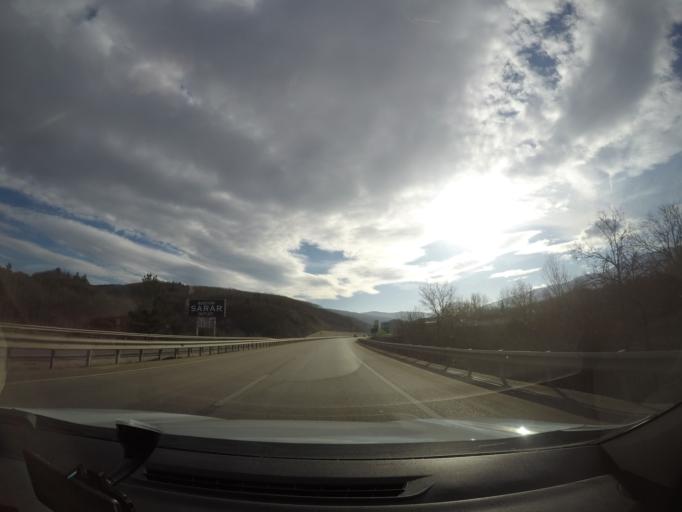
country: TR
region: Bursa
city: Tahtakopru
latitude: 39.9555
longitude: 29.6779
